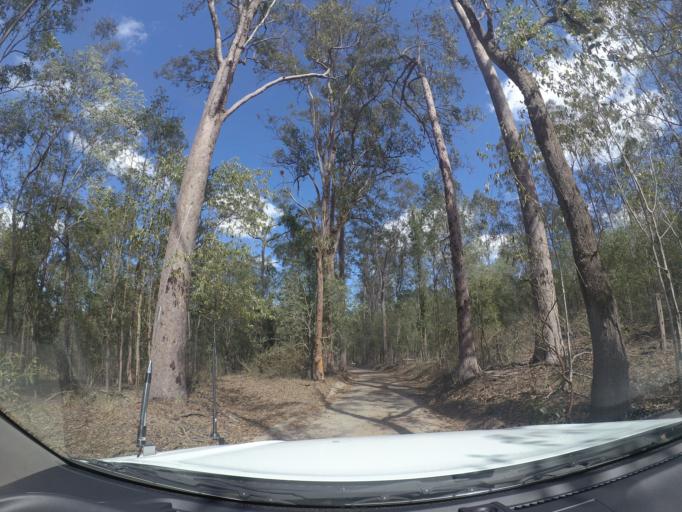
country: AU
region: Queensland
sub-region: Logan
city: Cedar Vale
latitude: -27.8381
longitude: 152.9724
